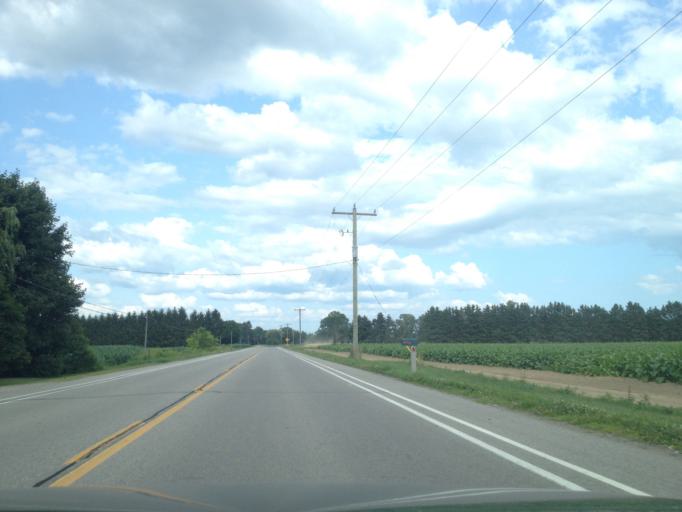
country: CA
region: Ontario
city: Aylmer
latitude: 42.6635
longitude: -80.9988
